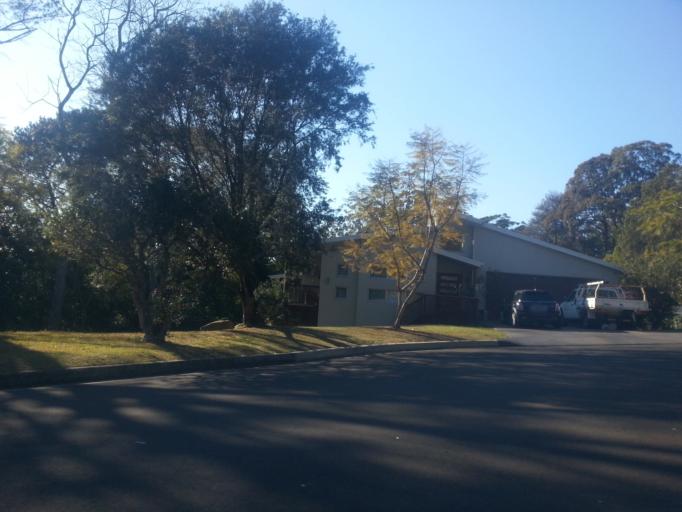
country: AU
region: New South Wales
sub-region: Wollongong
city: Bulli
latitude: -34.3193
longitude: 150.9101
